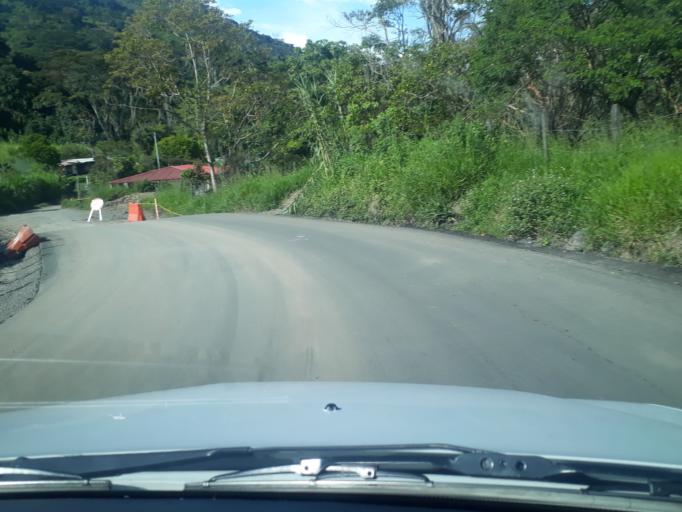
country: CO
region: Santander
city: Velez
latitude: 6.0498
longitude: -73.6519
